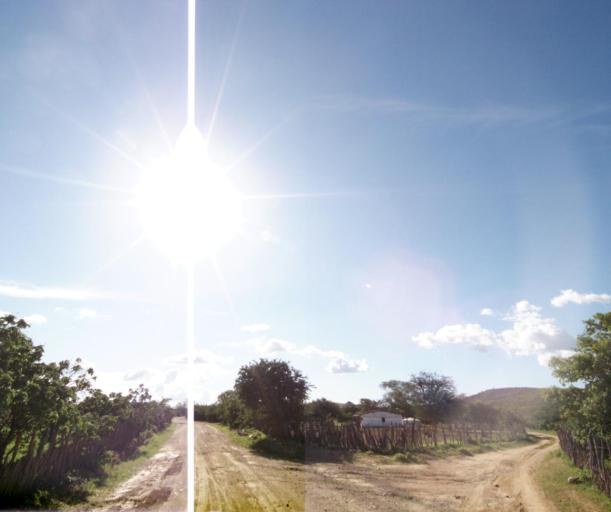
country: BR
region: Bahia
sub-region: Tanhacu
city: Tanhacu
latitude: -14.1871
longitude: -40.9516
